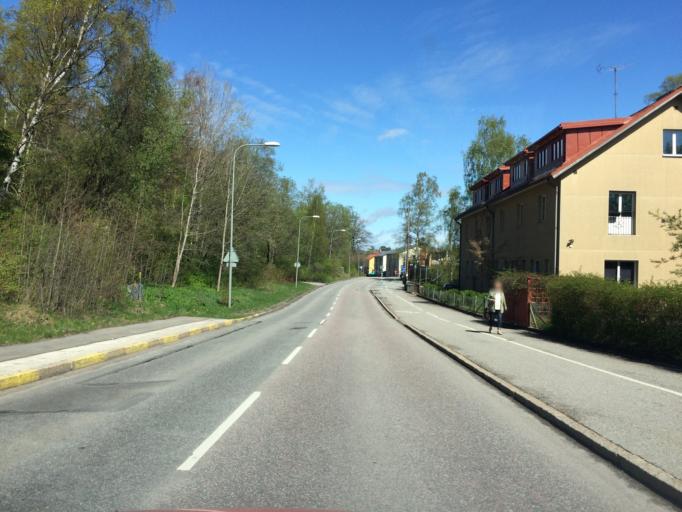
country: SE
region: Stockholm
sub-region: Huddinge Kommun
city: Segeltorp
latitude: 59.2984
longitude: 17.9567
